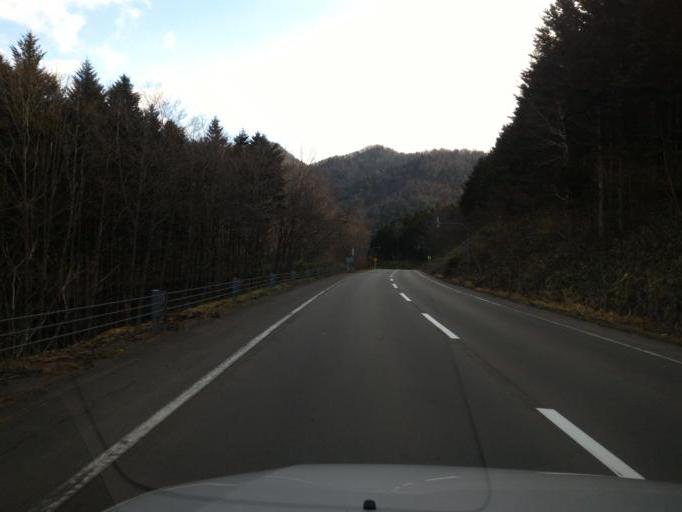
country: JP
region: Hokkaido
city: Shimo-furano
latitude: 43.3646
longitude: 142.2335
